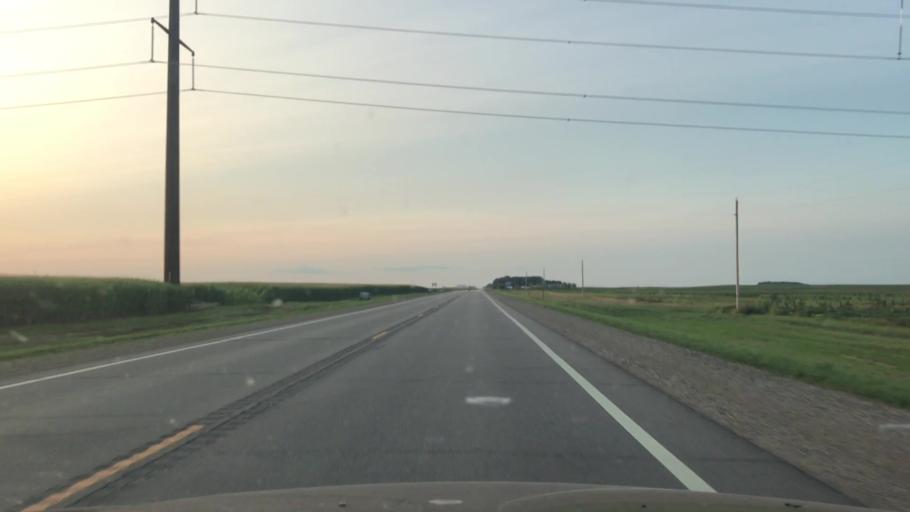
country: US
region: Minnesota
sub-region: Redwood County
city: Redwood Falls
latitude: 44.4338
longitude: -95.1176
